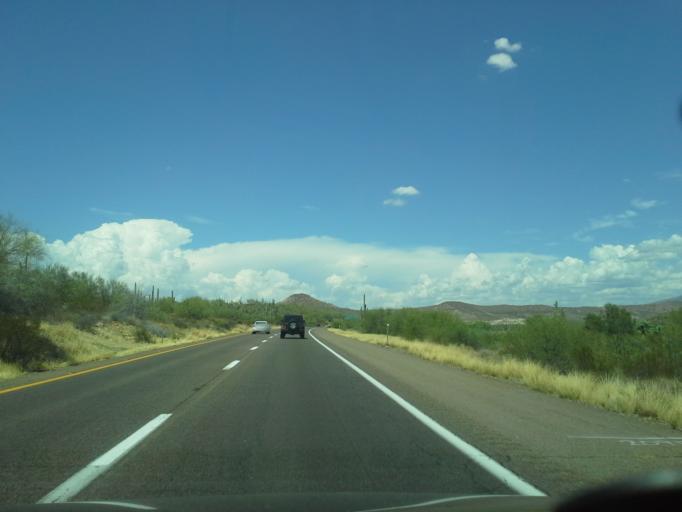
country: US
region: Arizona
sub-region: Maricopa County
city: New River
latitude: 33.9507
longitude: -112.1371
